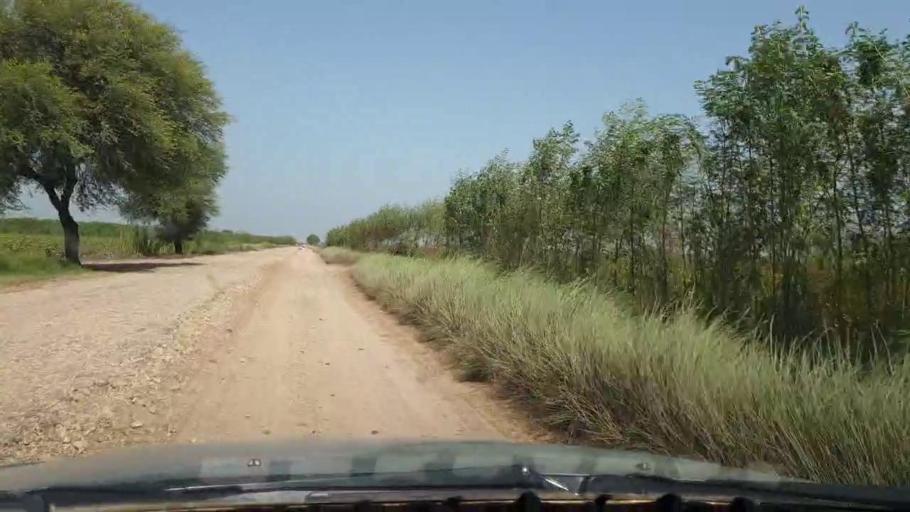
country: PK
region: Sindh
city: Tando Muhammad Khan
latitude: 25.1633
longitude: 68.6338
